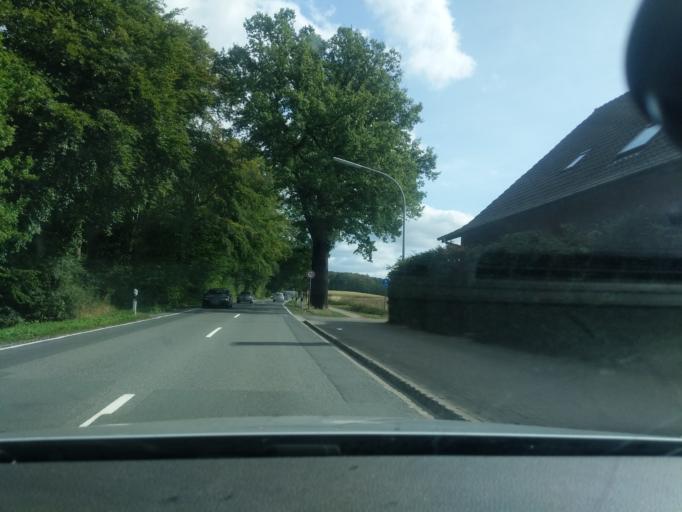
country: DE
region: Lower Saxony
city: Belm
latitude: 52.3093
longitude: 8.0968
